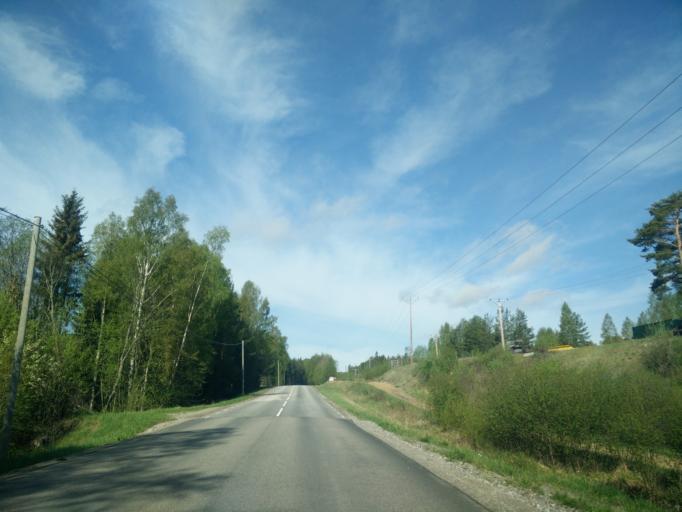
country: SE
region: Vaesternorrland
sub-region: Sundsvalls Kommun
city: Nolby
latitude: 62.2994
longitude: 17.3261
